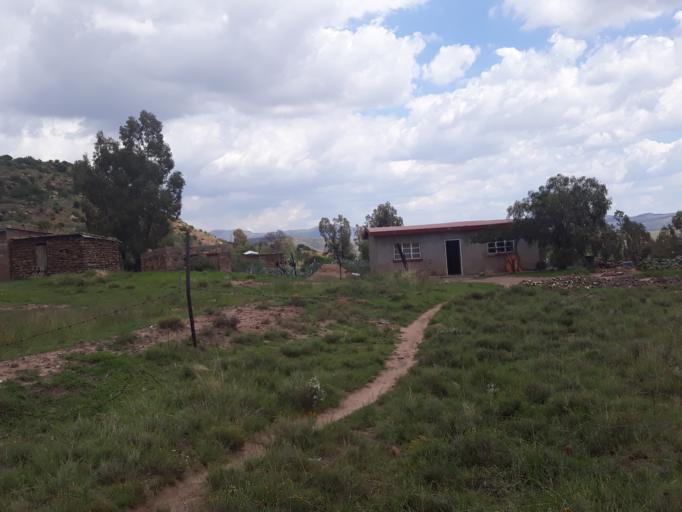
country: LS
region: Quthing
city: Quthing
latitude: -30.3400
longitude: 27.5345
